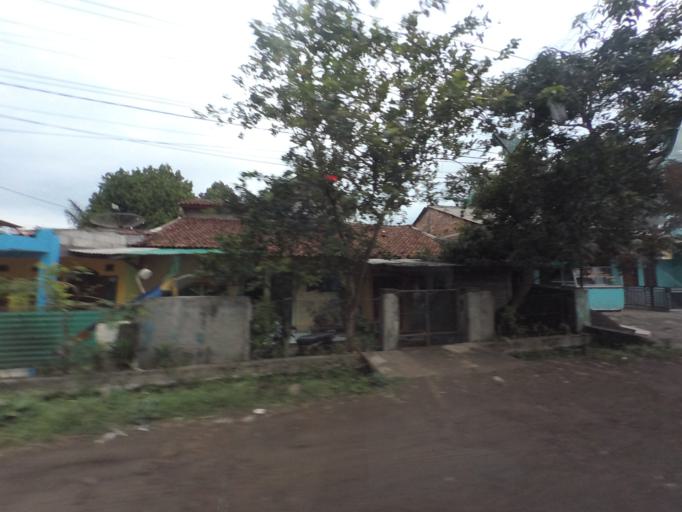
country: ID
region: West Java
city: Cicurug
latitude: -6.8370
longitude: 106.7604
